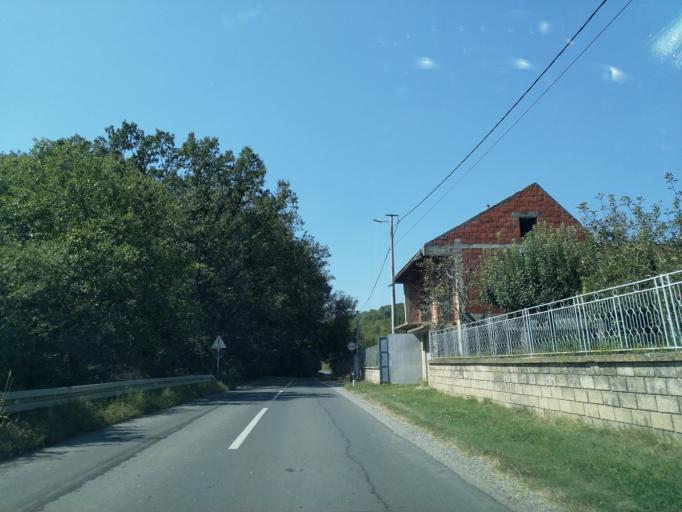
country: RS
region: Central Serbia
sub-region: Rasinski Okrug
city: Krusevac
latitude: 43.6210
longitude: 21.3187
